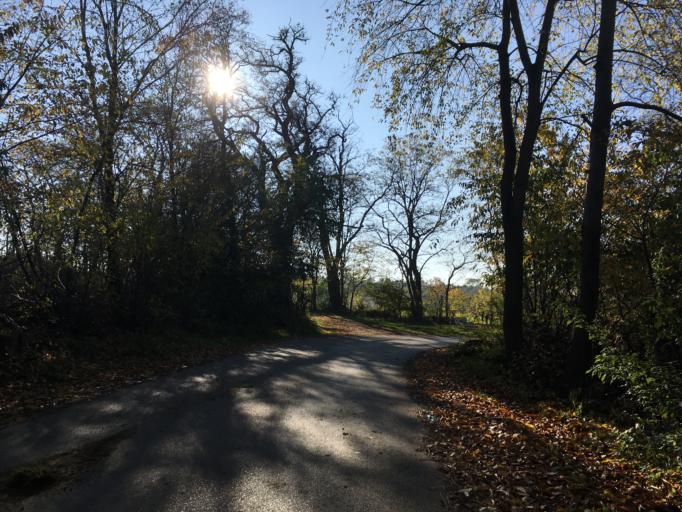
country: DE
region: Brandenburg
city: Reichenwalde
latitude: 52.2892
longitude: 14.0207
